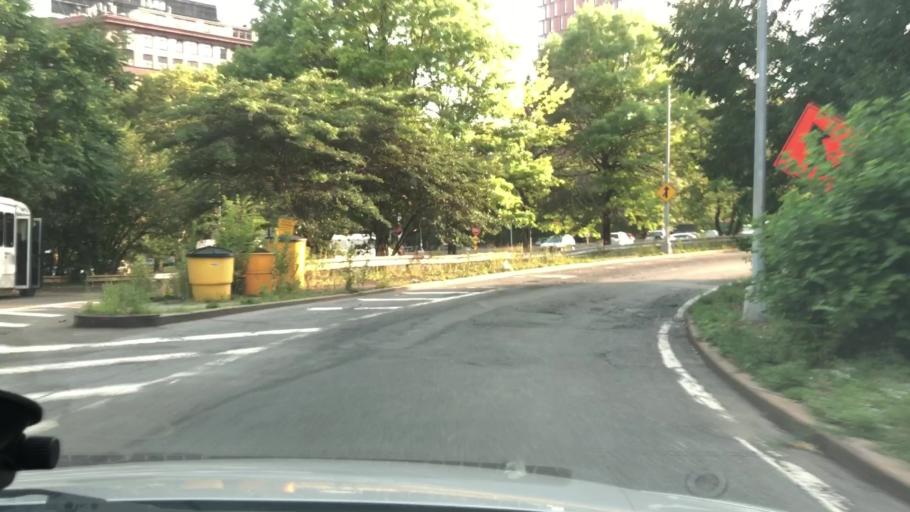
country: US
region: New York
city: New York City
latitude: 40.6989
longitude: -73.9847
